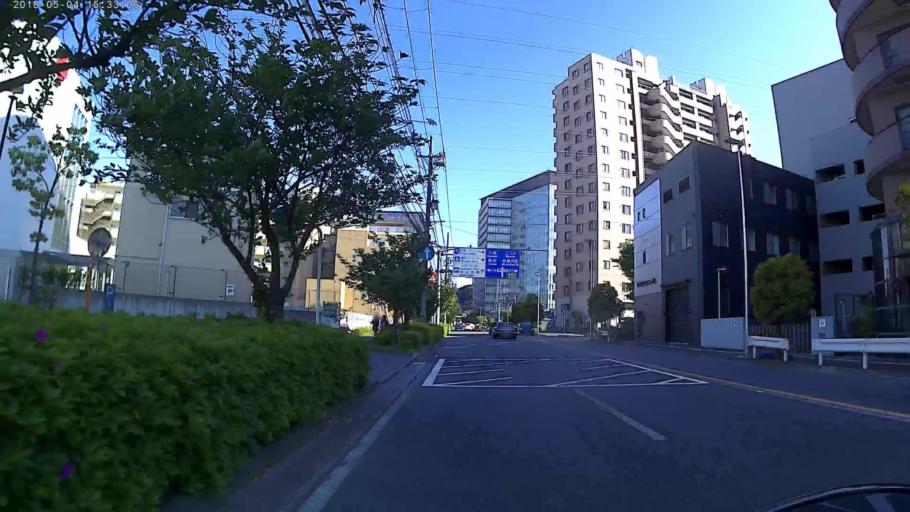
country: JP
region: Kanagawa
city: Yokohama
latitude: 35.5140
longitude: 139.6213
